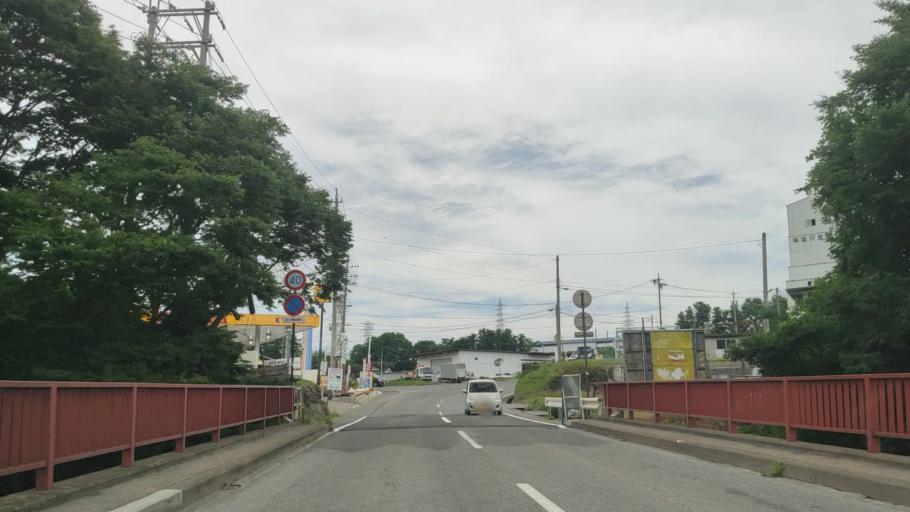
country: JP
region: Nagano
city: Kamimaruko
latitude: 36.3413
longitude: 138.3521
